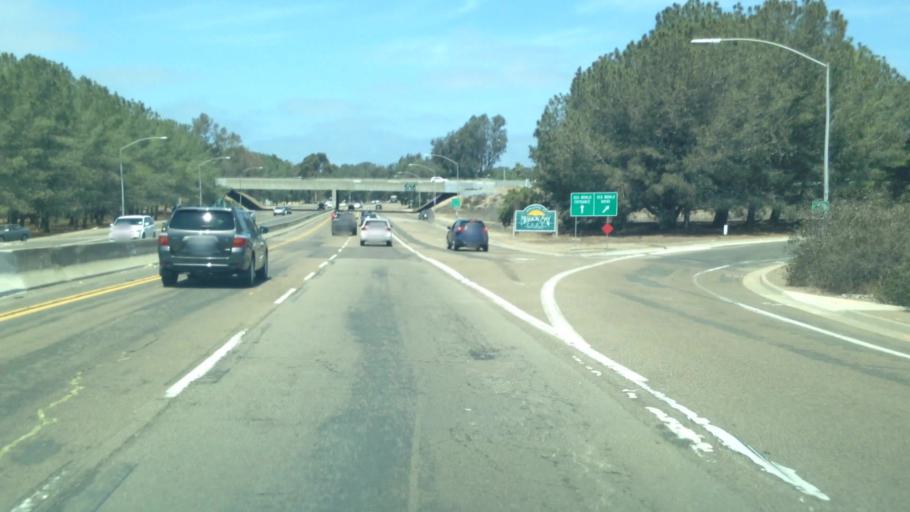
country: US
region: California
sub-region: San Diego County
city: San Diego
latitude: 32.7601
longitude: -117.2280
